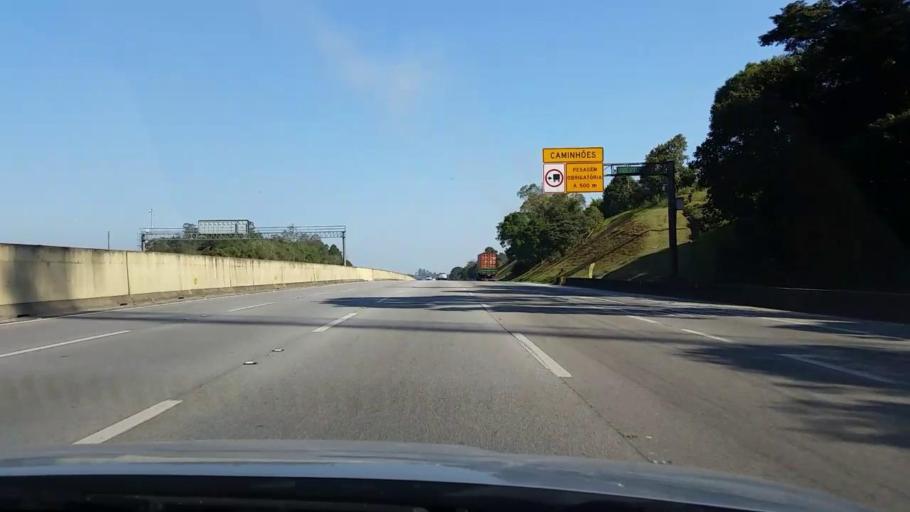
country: BR
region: Sao Paulo
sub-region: Sao Bernardo Do Campo
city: Sao Bernardo do Campo
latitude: -23.7761
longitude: -46.5955
